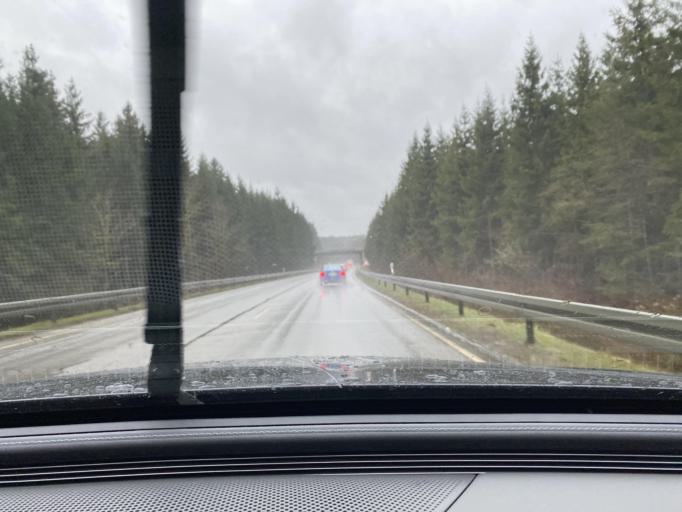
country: DE
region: Baden-Wuerttemberg
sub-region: Freiburg Region
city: Deisslingen
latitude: 48.0829
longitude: 8.5993
